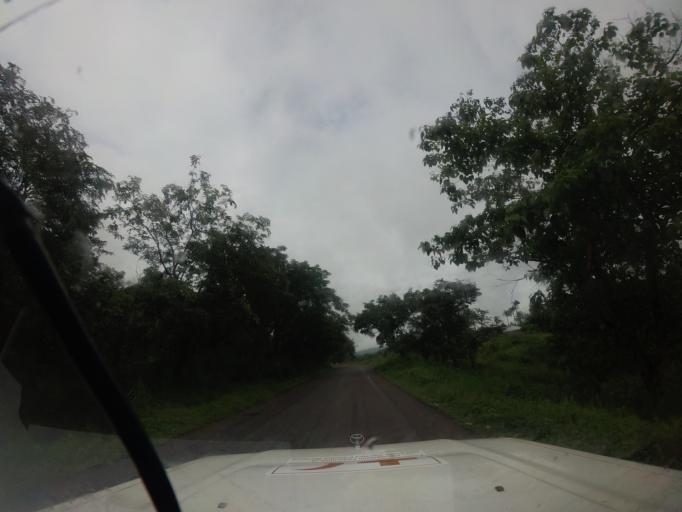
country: SL
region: Northern Province
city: Bumbuna
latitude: 9.3482
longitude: -11.8205
